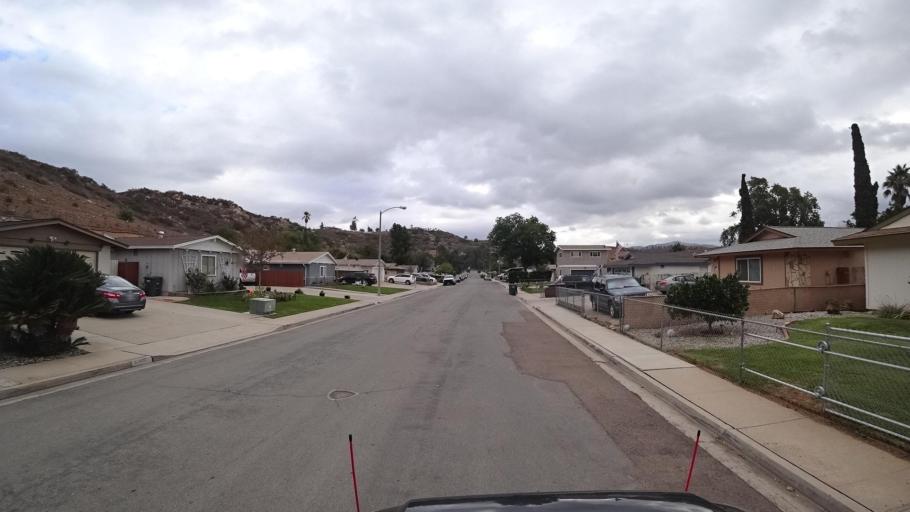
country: US
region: California
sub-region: San Diego County
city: Lakeside
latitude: 32.8657
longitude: -116.9122
